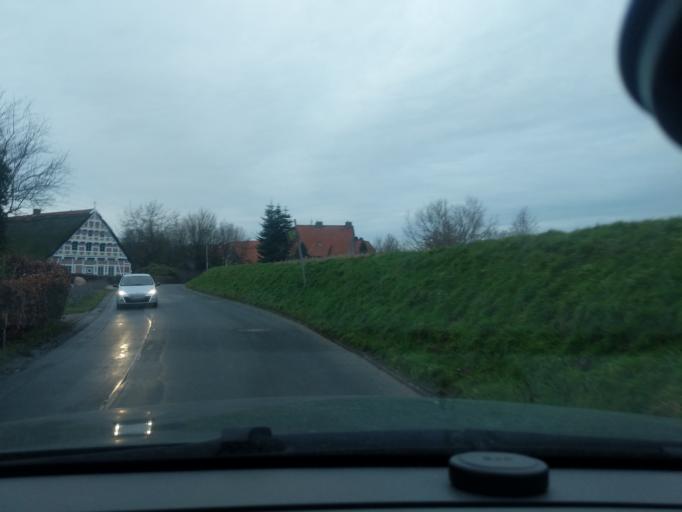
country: DE
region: Lower Saxony
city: Mittelnkirchen
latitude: 53.5367
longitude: 9.6121
